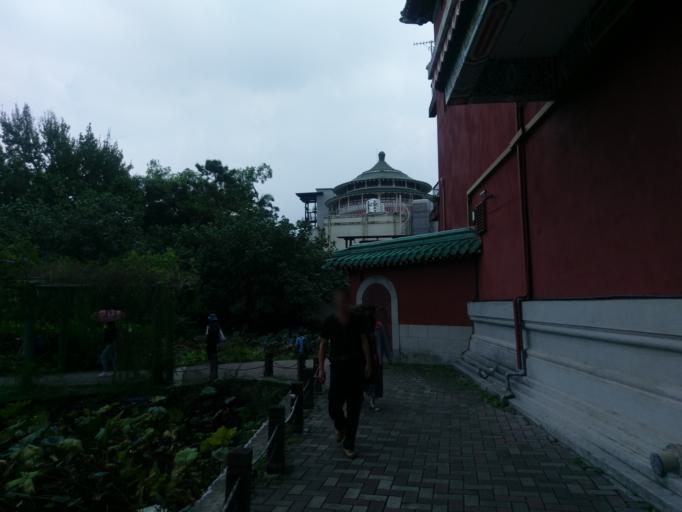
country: TW
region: Taipei
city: Taipei
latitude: 25.0317
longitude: 121.5112
